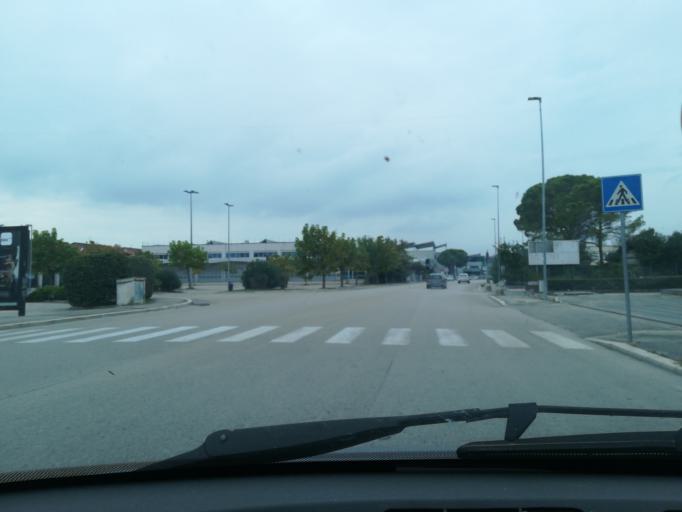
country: IT
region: The Marches
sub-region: Provincia di Macerata
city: Piediripa
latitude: 43.2781
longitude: 13.5040
